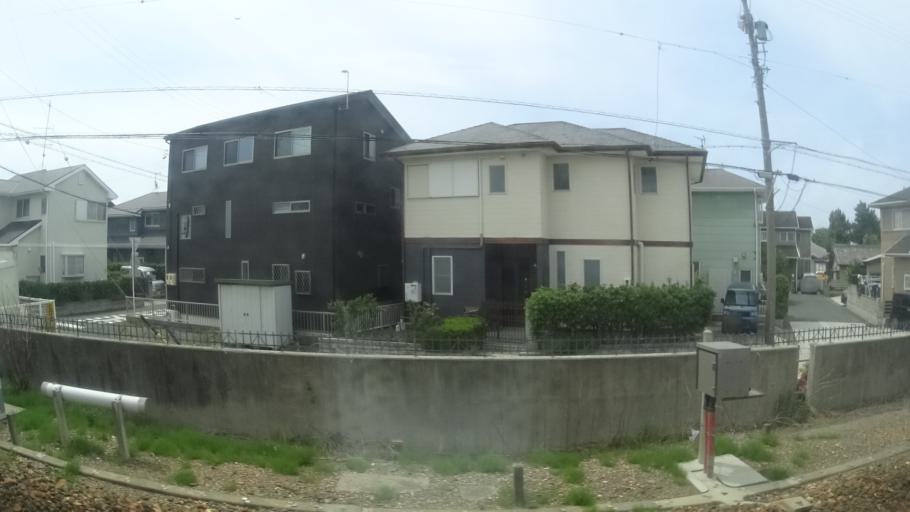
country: JP
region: Shizuoka
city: Hamamatsu
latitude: 34.6853
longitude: 137.6533
